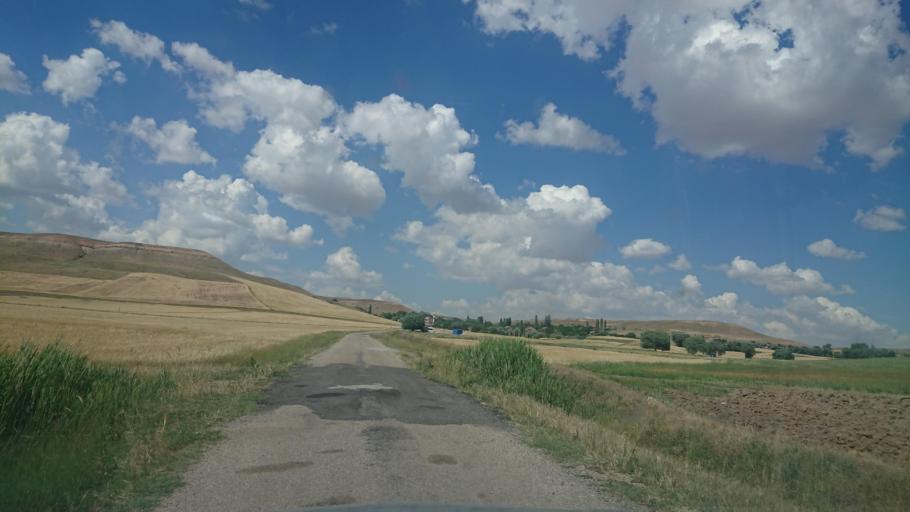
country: TR
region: Aksaray
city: Agacoren
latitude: 38.7959
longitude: 33.8225
